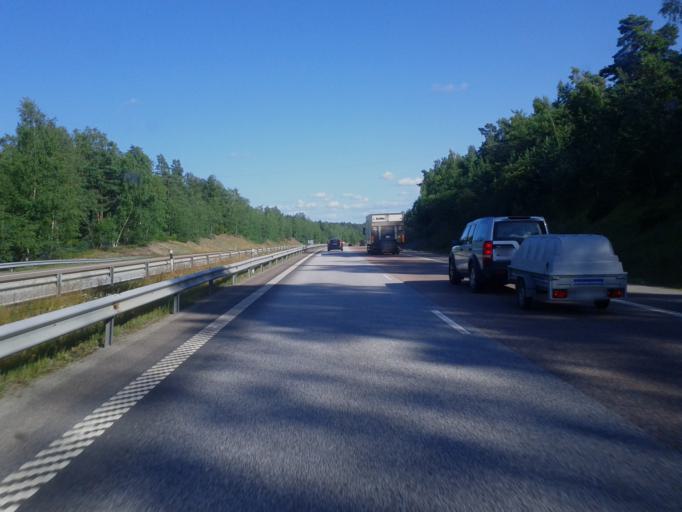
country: SE
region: Uppsala
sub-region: Habo Kommun
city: Balsta
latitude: 59.5791
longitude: 17.5337
